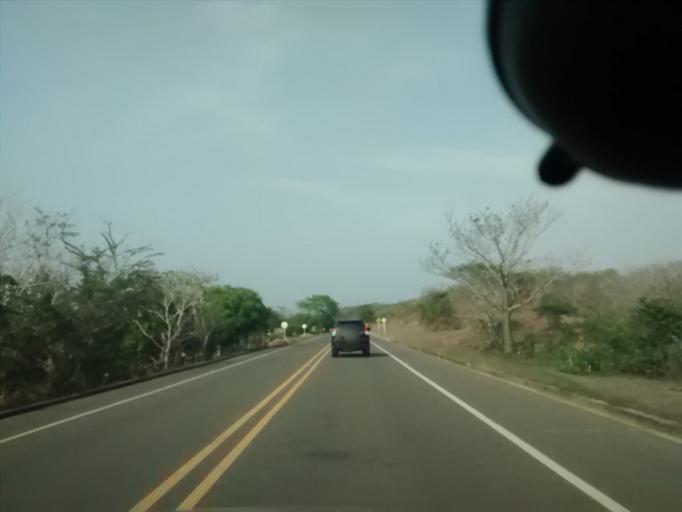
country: CO
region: Bolivar
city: Clemencia
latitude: 10.6383
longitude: -75.4099
